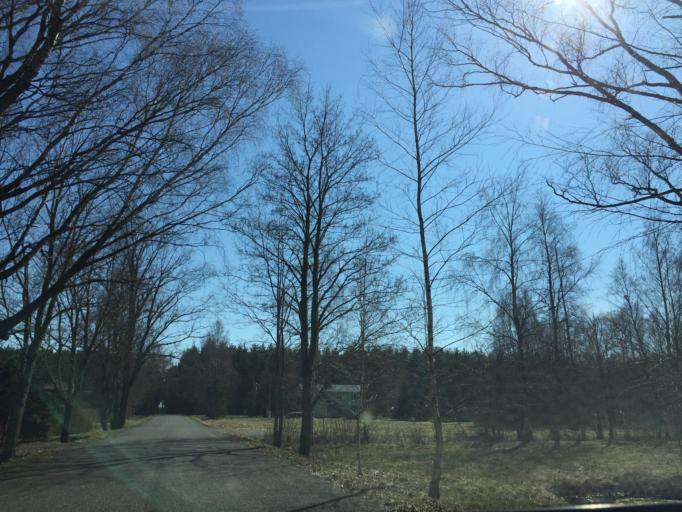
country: EE
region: Jogevamaa
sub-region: Mustvee linn
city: Mustvee
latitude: 58.9942
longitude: 27.2267
